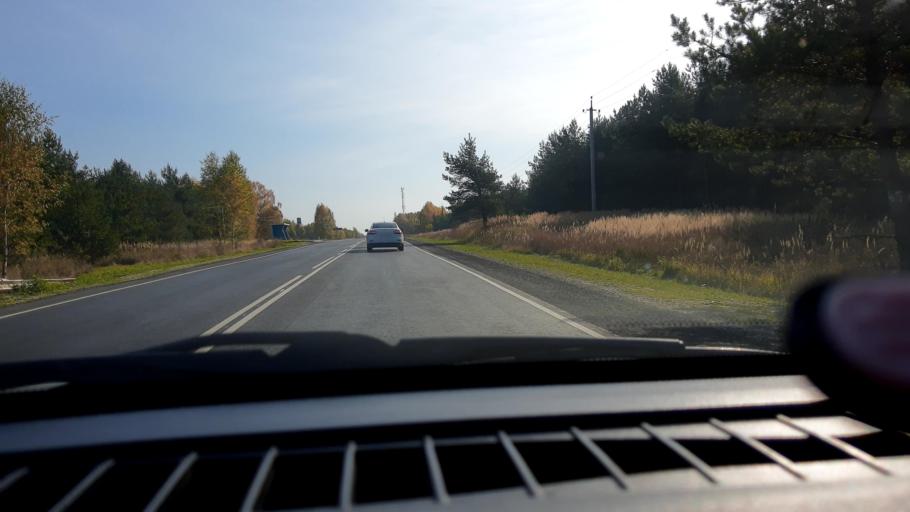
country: RU
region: Nizjnij Novgorod
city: Novaya Balakhna
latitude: 56.6047
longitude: 43.6214
